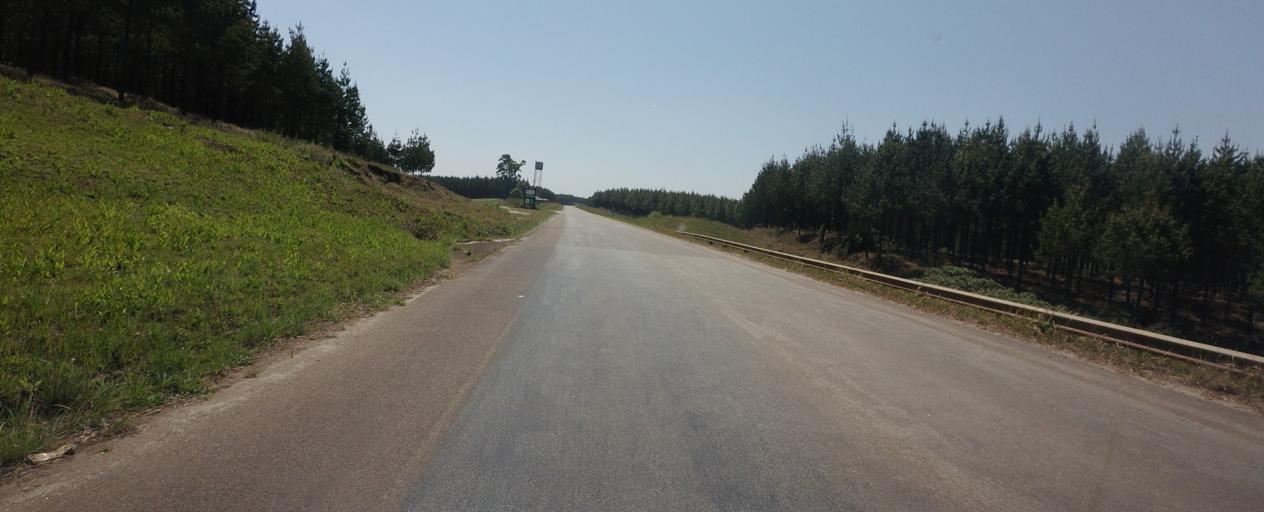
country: ZA
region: Mpumalanga
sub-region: Ehlanzeni District
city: Graksop
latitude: -24.9062
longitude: 30.8451
